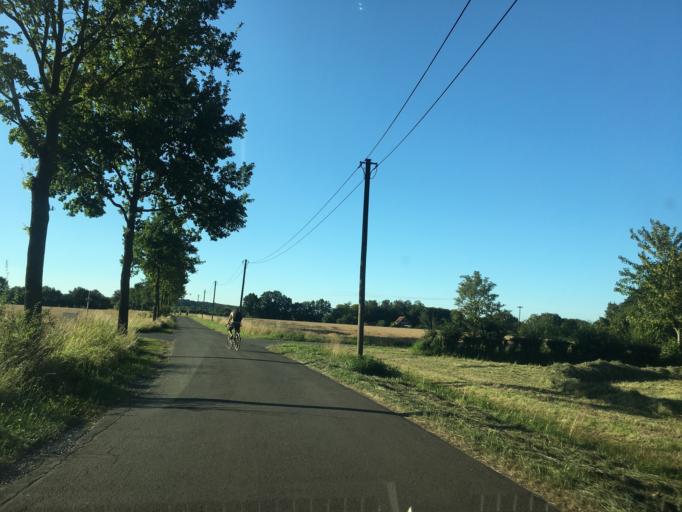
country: DE
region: North Rhine-Westphalia
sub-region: Regierungsbezirk Munster
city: Muenster
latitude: 51.9933
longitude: 7.5745
